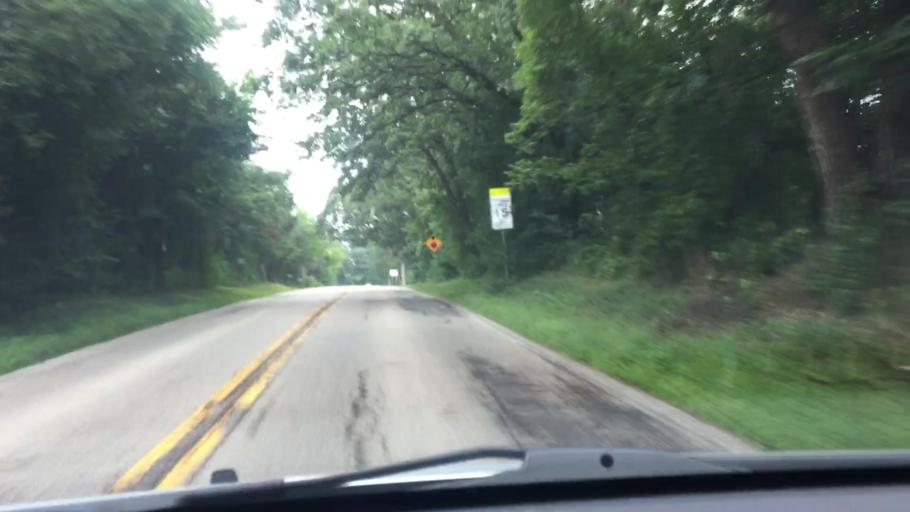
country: US
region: Wisconsin
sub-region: Waukesha County
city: Dousman
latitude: 43.0237
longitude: -88.4428
